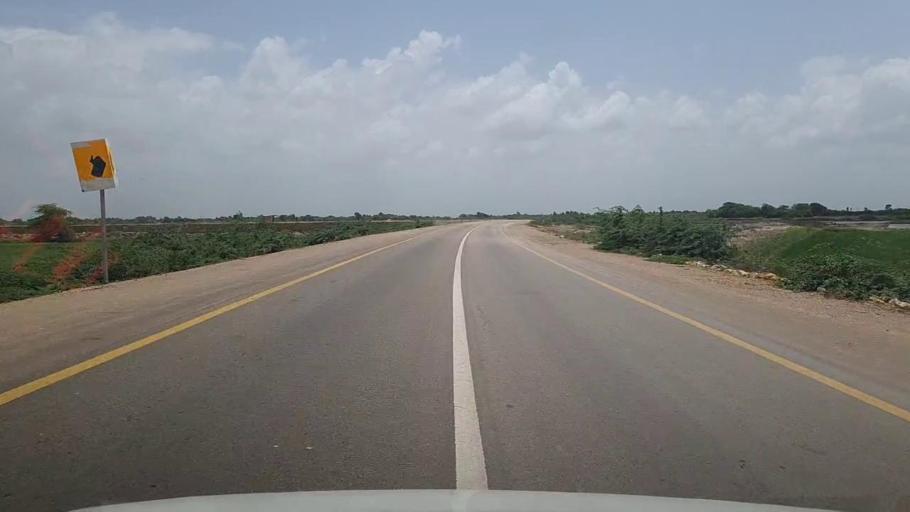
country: PK
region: Sindh
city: Thatta
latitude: 24.7588
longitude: 67.9520
